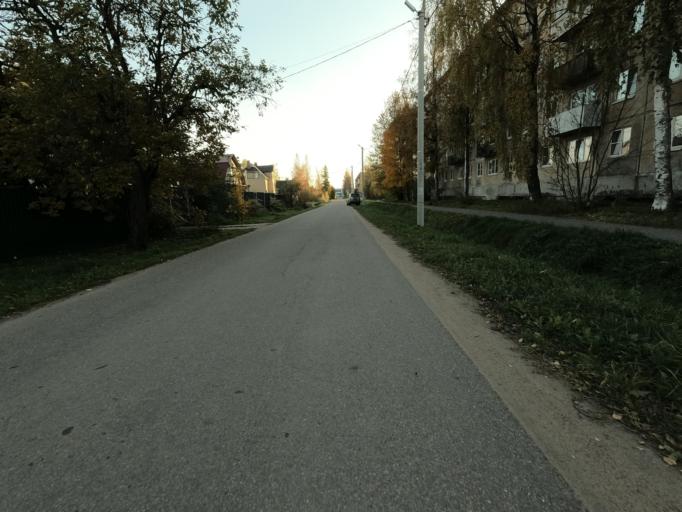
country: RU
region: Leningrad
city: Mga
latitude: 59.7589
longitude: 31.0691
